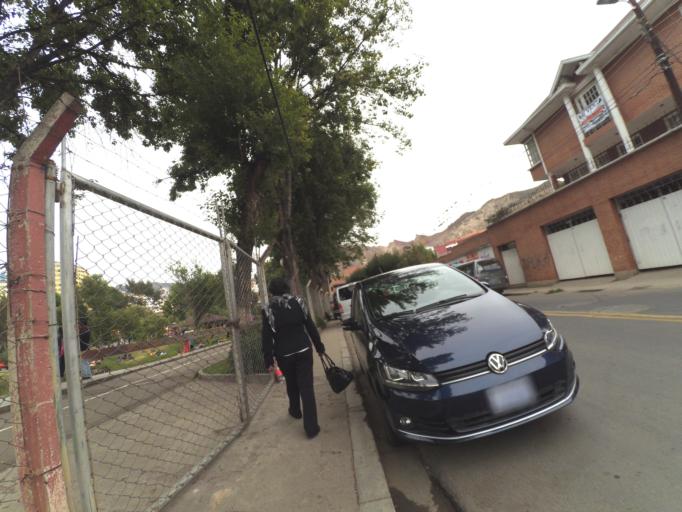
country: BO
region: La Paz
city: La Paz
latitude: -16.5420
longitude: -68.0652
